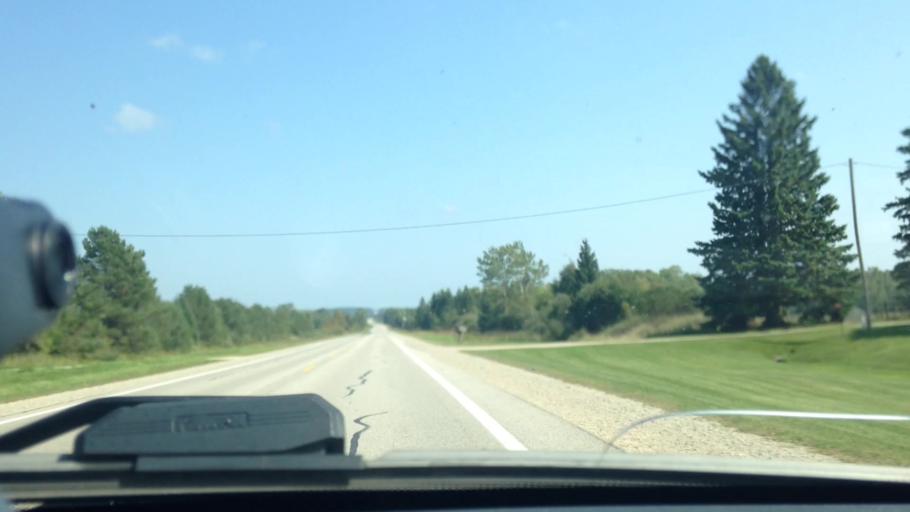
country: US
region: Michigan
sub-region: Luce County
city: Newberry
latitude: 46.3102
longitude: -85.6295
